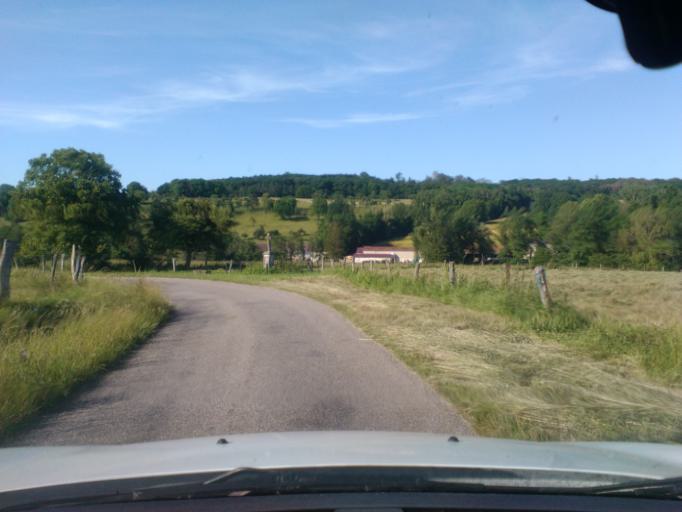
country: FR
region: Lorraine
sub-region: Departement des Vosges
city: Mirecourt
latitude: 48.2634
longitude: 6.2287
